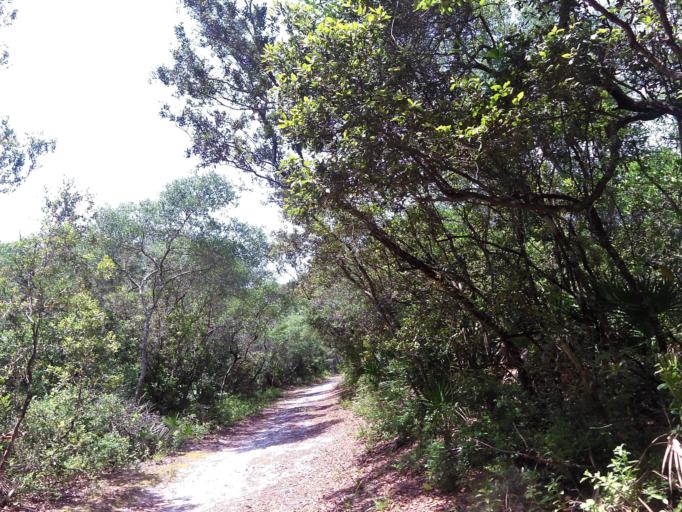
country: US
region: Florida
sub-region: Nassau County
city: Fernandina Beach
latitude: 30.4981
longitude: -81.4931
